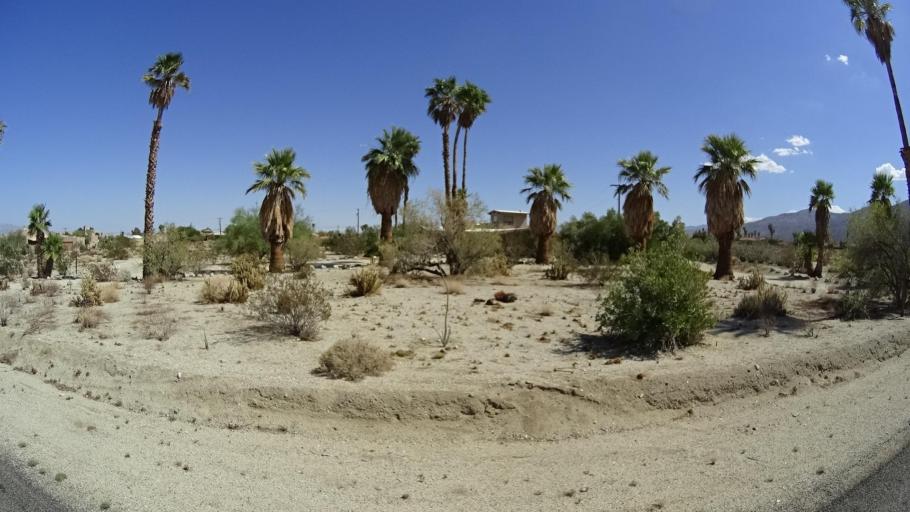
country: US
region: California
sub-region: San Diego County
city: Borrego Springs
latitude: 33.2320
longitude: -116.3878
